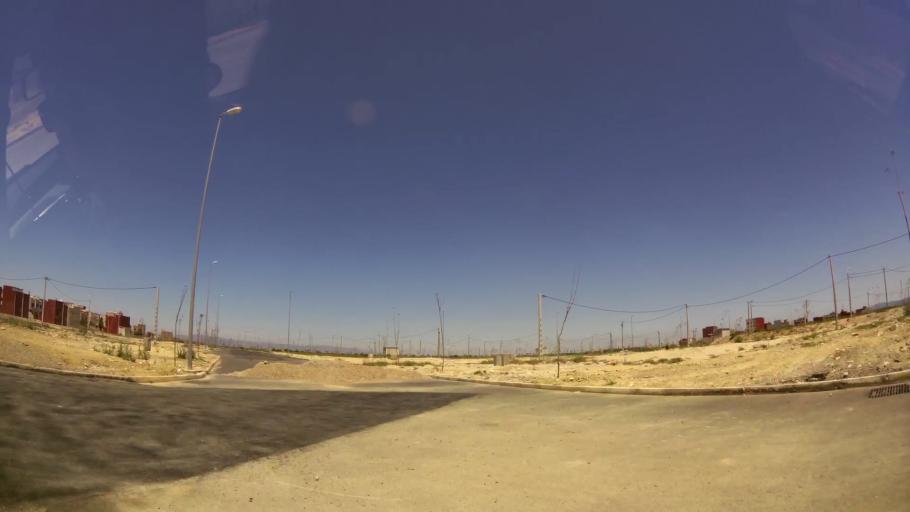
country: MA
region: Oriental
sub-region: Oujda-Angad
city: Oujda
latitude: 34.6798
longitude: -1.8628
